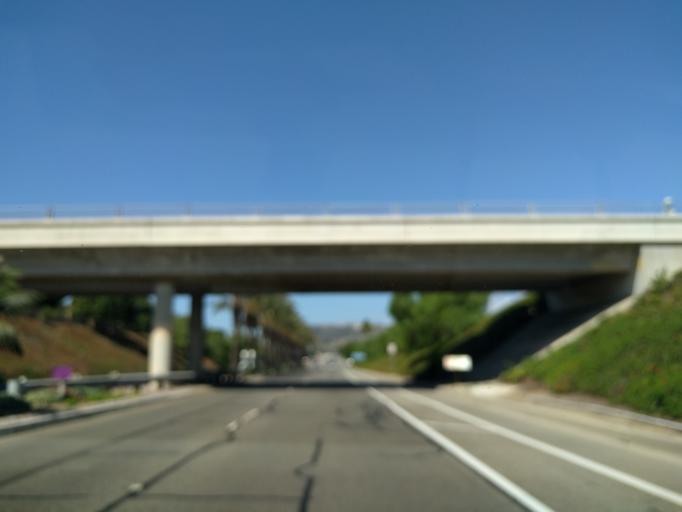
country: US
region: California
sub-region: Orange County
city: Dana Point
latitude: 33.4736
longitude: -117.7151
